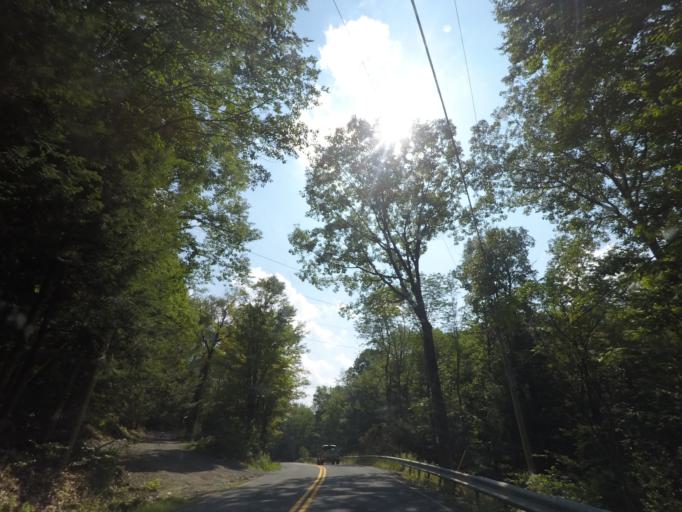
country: US
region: New York
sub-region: Rensselaer County
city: Poestenkill
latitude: 42.7076
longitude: -73.5118
